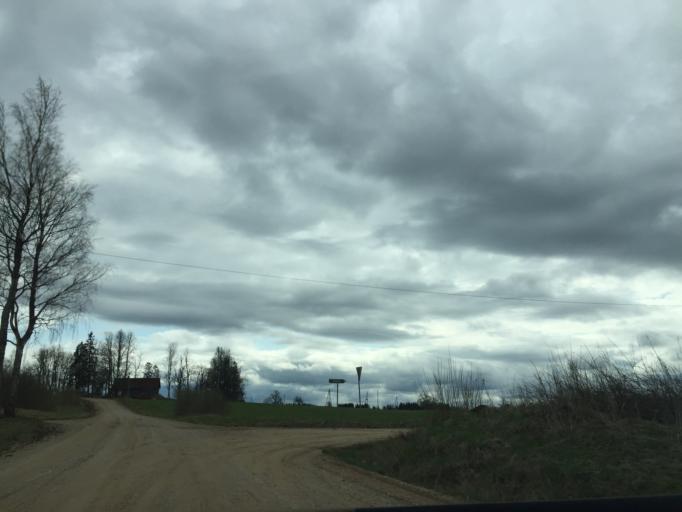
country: LV
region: Jaunpiebalga
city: Jaunpiebalga
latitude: 57.1535
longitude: 26.0684
